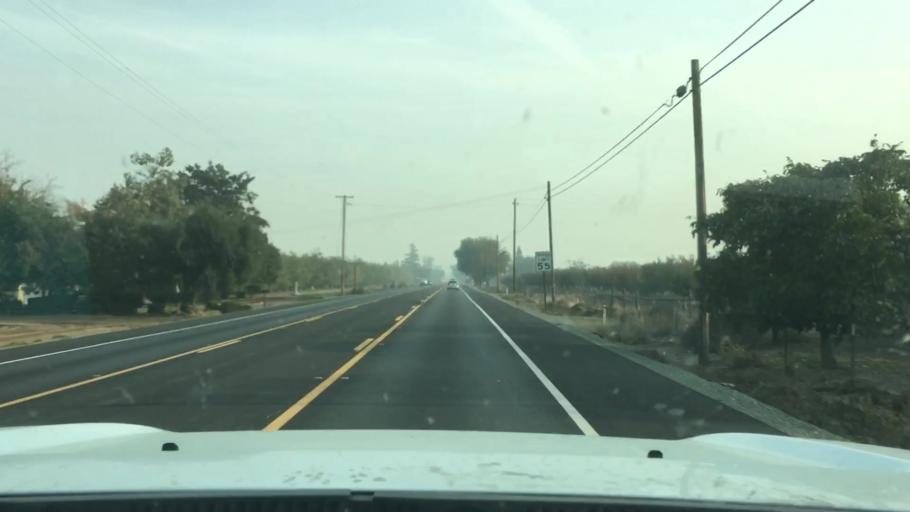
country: US
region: California
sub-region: San Joaquin County
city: August
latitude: 37.9933
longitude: -121.2368
